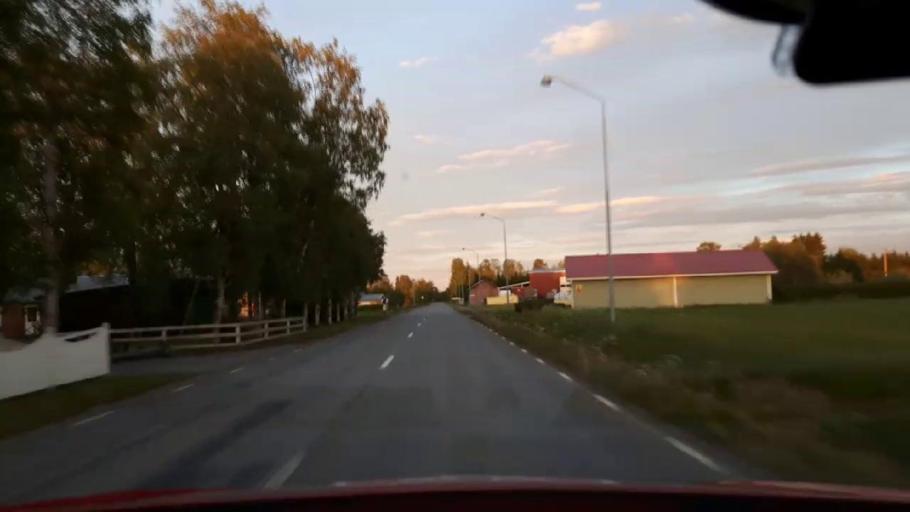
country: SE
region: Jaemtland
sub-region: OEstersunds Kommun
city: Ostersund
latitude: 63.1178
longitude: 14.7206
